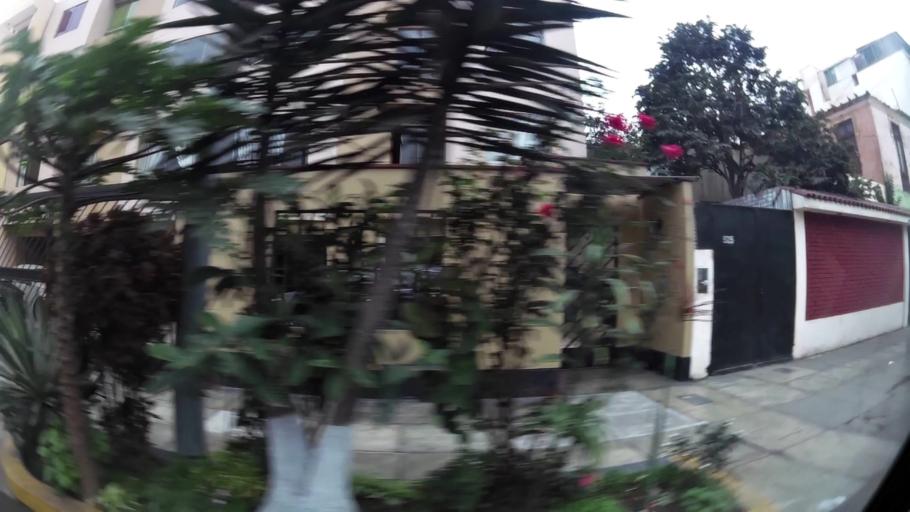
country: PE
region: Lima
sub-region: Lima
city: San Isidro
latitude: -12.0917
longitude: -77.0807
